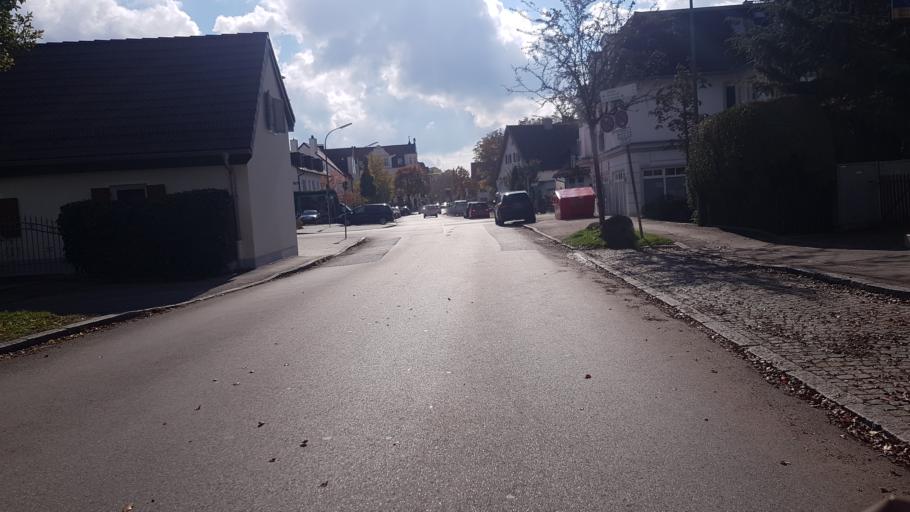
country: DE
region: Bavaria
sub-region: Upper Bavaria
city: Neuried
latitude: 48.1168
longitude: 11.4795
